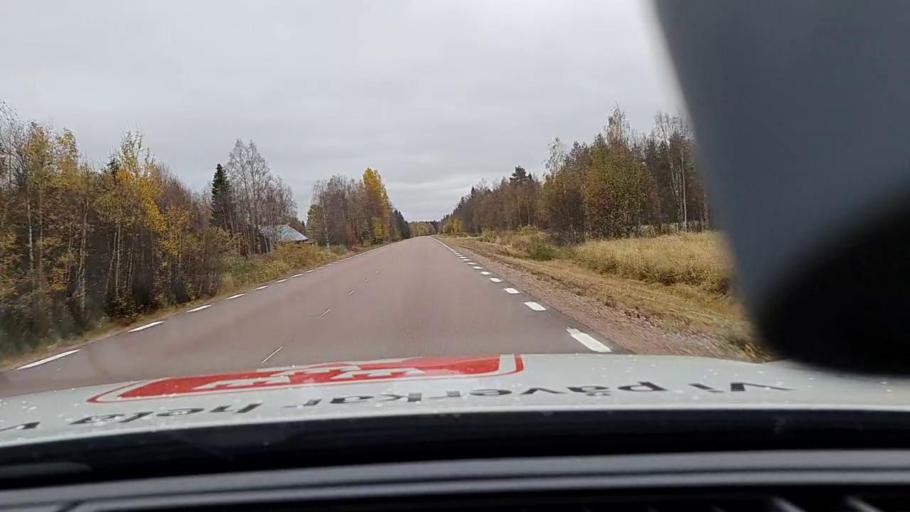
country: FI
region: Lapland
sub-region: Kemi-Tornio
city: Tornio
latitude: 66.0556
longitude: 23.9342
